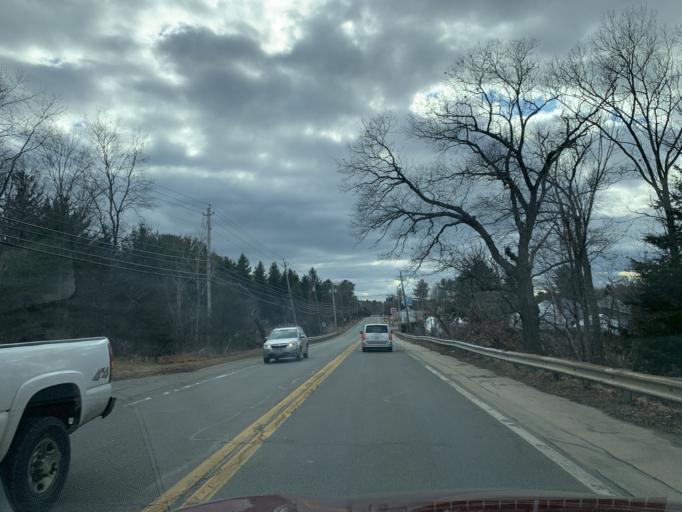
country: US
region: Massachusetts
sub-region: Essex County
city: Newburyport
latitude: 42.7878
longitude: -70.8794
